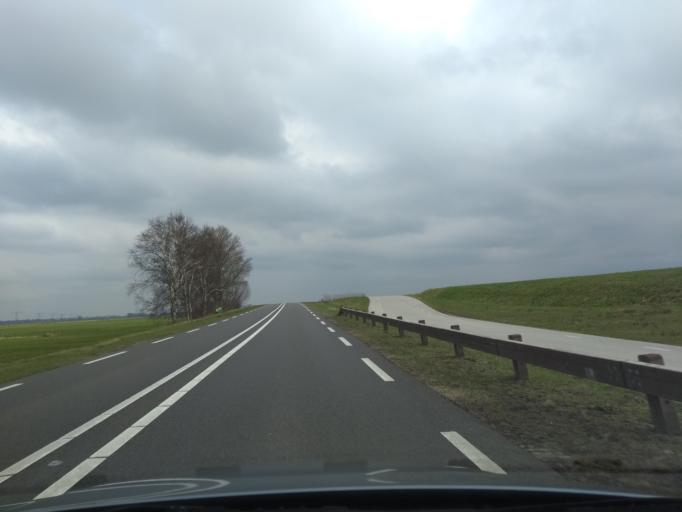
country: NL
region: Overijssel
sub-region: Gemeente Steenwijkerland
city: Sint Jansklooster
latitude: 52.6498
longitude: 6.0156
